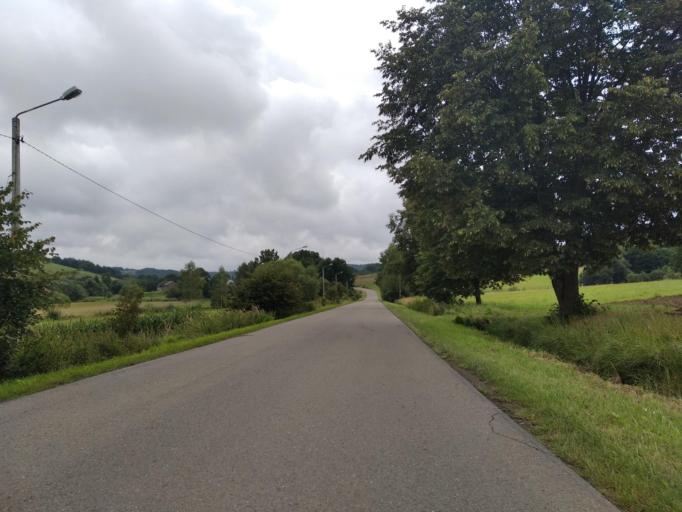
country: PL
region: Subcarpathian Voivodeship
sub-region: Powiat brzozowski
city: Nozdrzec
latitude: 49.7315
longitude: 22.2713
